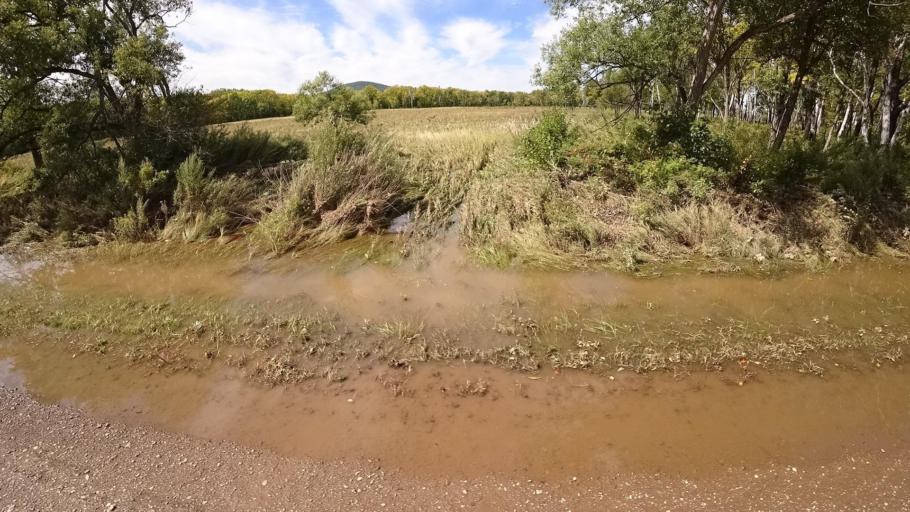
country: RU
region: Primorskiy
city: Yakovlevka
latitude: 44.6628
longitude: 133.7504
